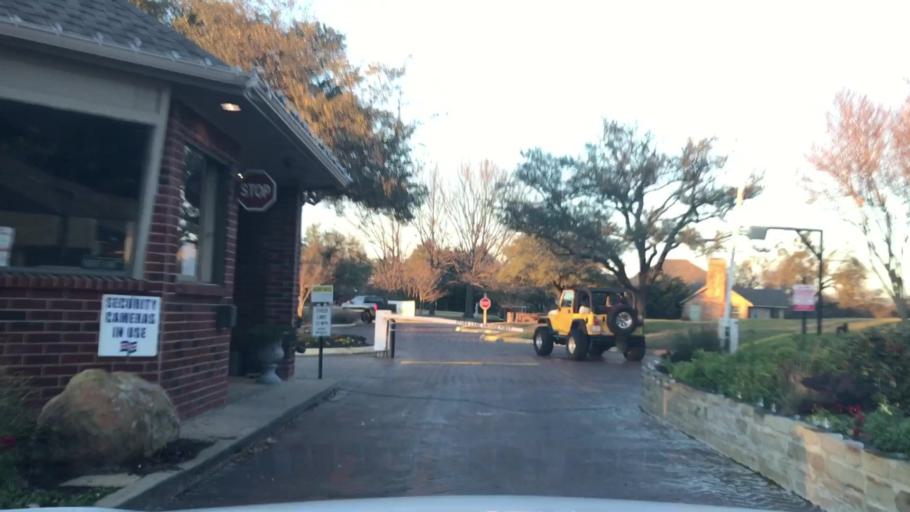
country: US
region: Texas
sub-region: Rockwall County
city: Heath
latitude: 32.8764
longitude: -96.4760
